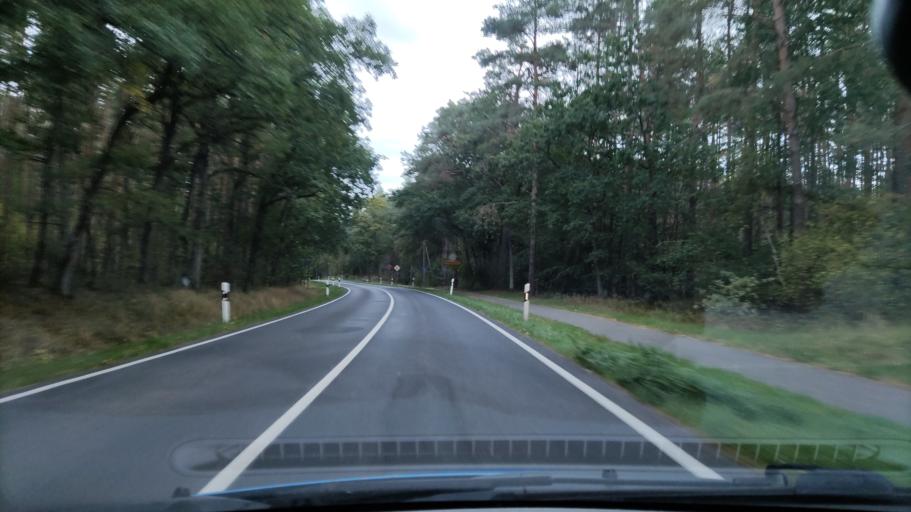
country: DE
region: Mecklenburg-Vorpommern
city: Lubtheen
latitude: 53.3796
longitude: 10.9675
